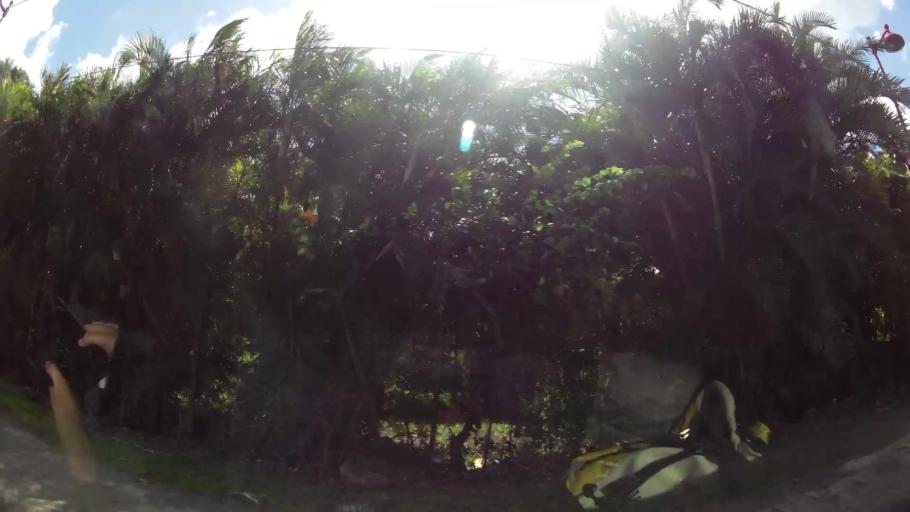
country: MQ
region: Martinique
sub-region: Martinique
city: Saint-Pierre
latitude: 14.6988
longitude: -61.1783
